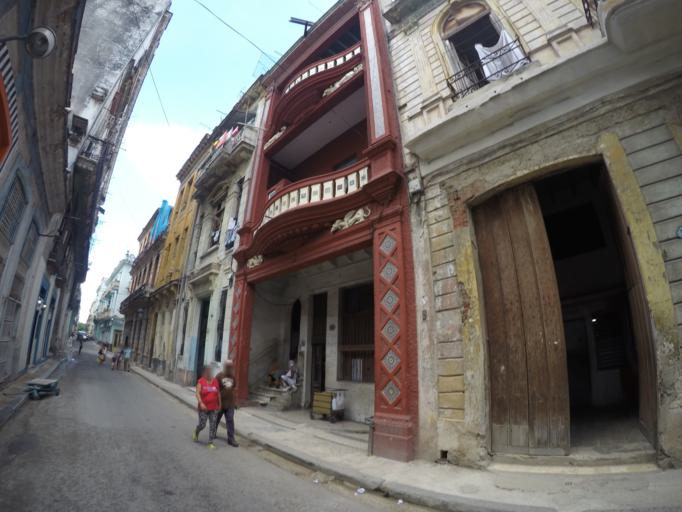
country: CU
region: La Habana
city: La Habana Vieja
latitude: 23.1402
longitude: -82.3526
